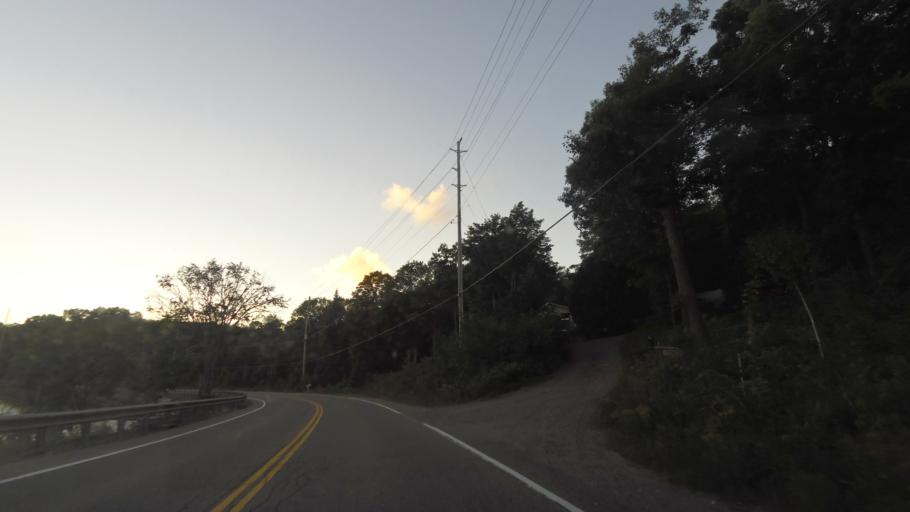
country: CA
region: Ontario
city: Bancroft
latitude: 45.0233
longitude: -78.3712
